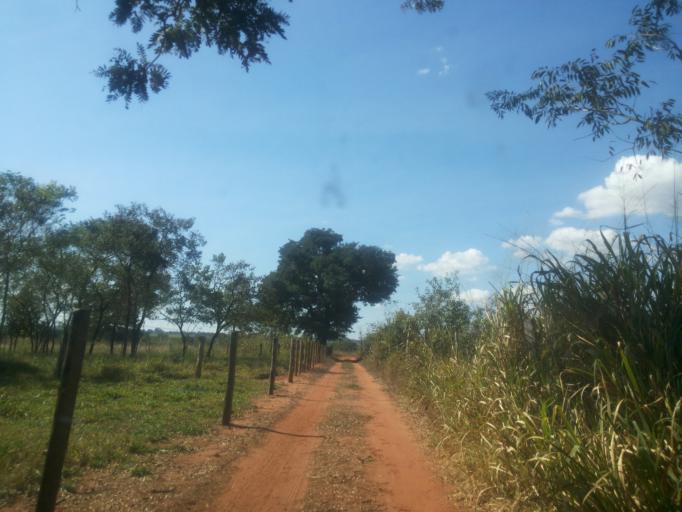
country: BR
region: Minas Gerais
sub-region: Santa Vitoria
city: Santa Vitoria
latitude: -18.9943
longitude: -50.3757
